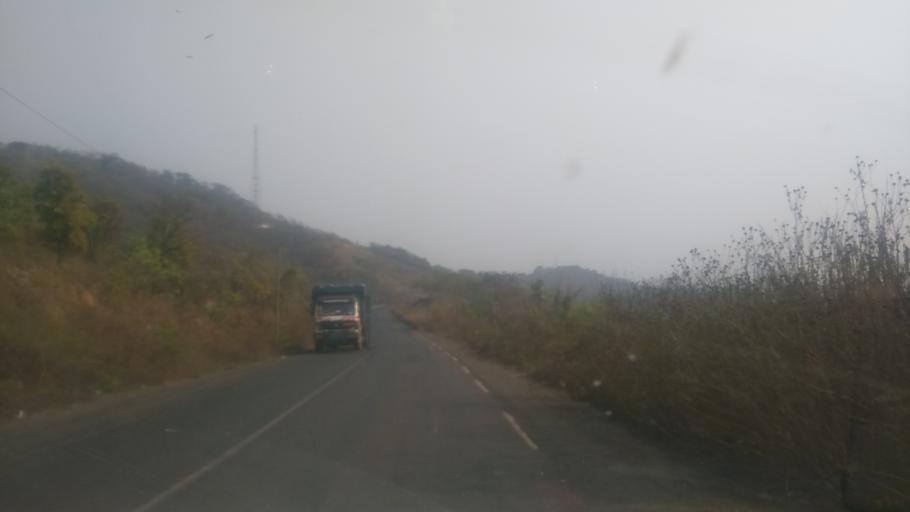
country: CM
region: West
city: Tonga
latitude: 5.0451
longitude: 10.7003
